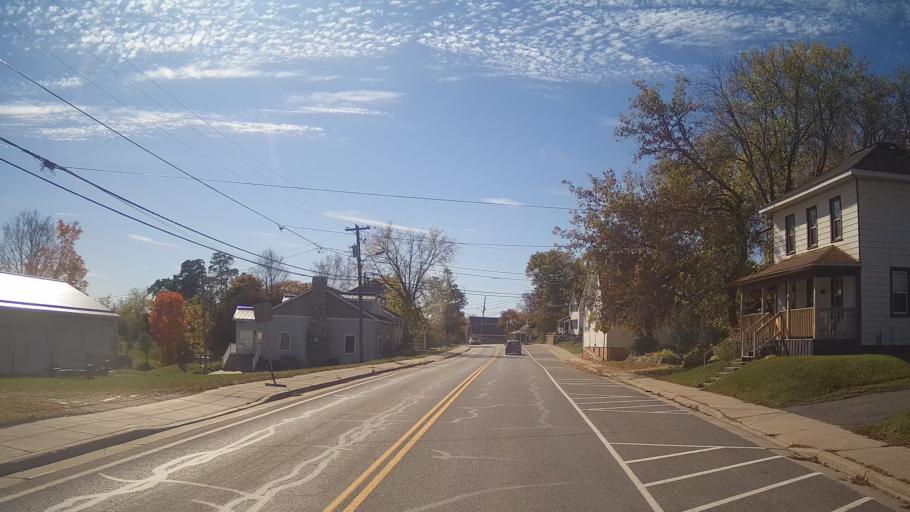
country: CA
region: Ontario
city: Perth
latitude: 44.7714
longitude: -76.6876
